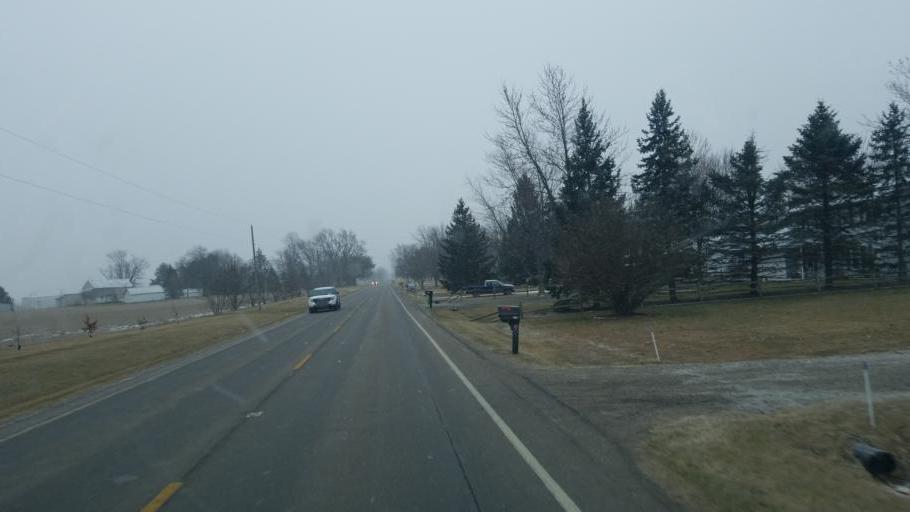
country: US
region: Ohio
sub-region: Defiance County
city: Hicksville
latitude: 41.3068
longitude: -84.7814
